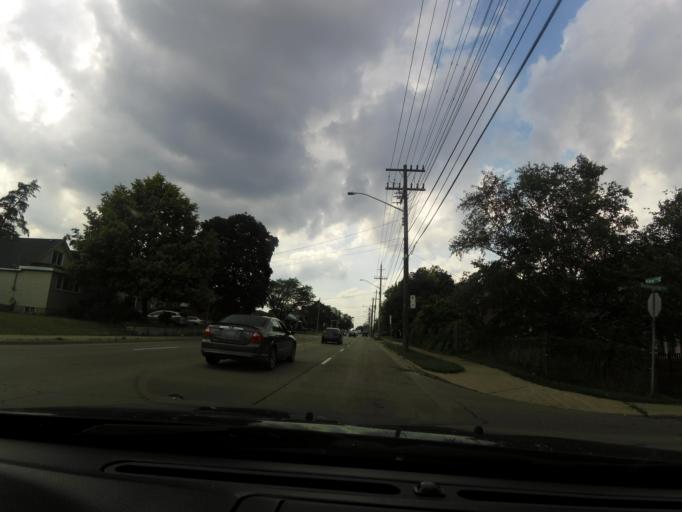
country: CA
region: Ontario
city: Hamilton
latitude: 43.2297
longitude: -79.7968
